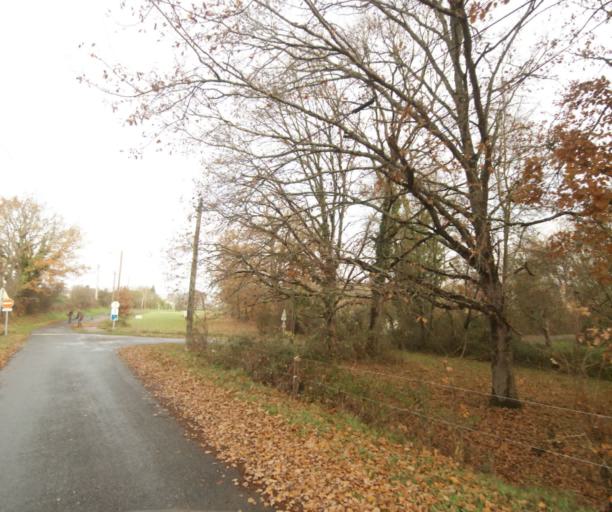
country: FR
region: Midi-Pyrenees
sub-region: Departement de la Haute-Garonne
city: Villemur-sur-Tarn
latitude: 43.8526
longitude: 1.4902
